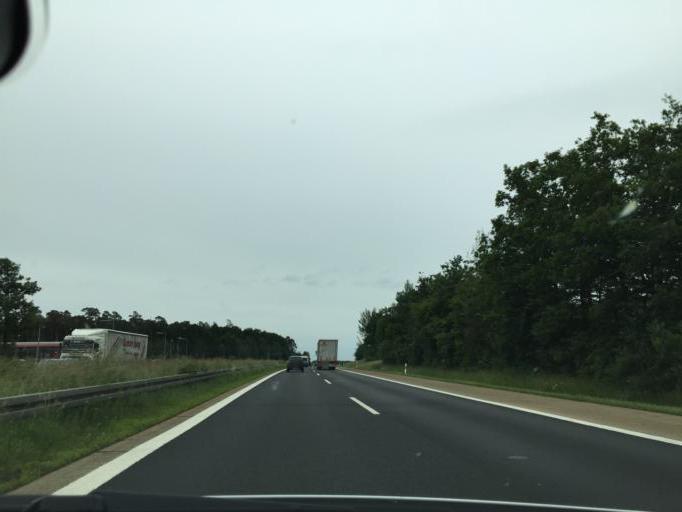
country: DE
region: Bavaria
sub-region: Regierungsbezirk Unterfranken
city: Schondra
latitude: 50.2664
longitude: 9.8815
